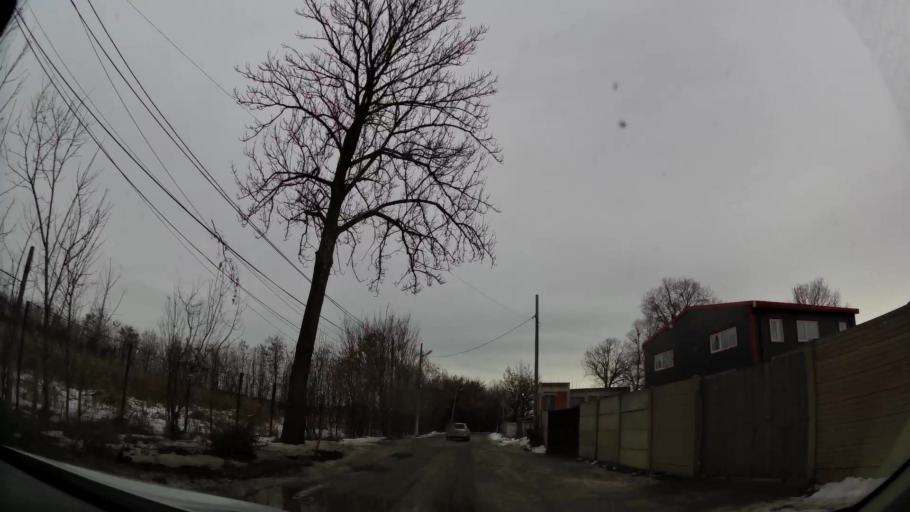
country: RO
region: Ilfov
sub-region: Comuna Pantelimon
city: Pantelimon
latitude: 44.4658
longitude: 26.2101
